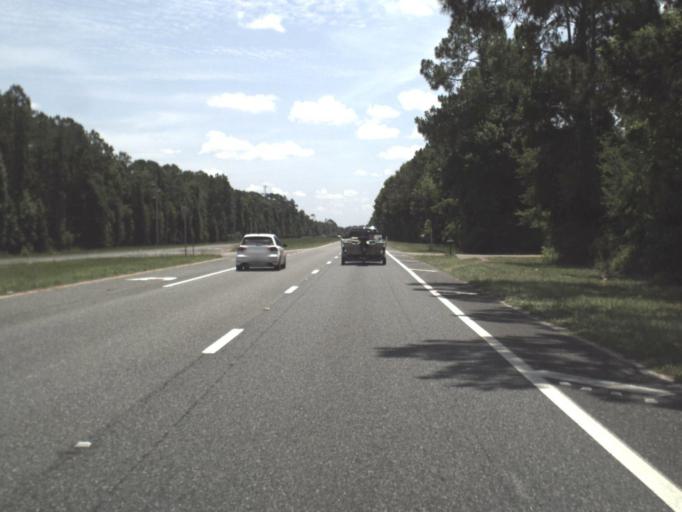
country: US
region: Florida
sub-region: Dixie County
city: Cross City
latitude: 29.6479
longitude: -83.1585
